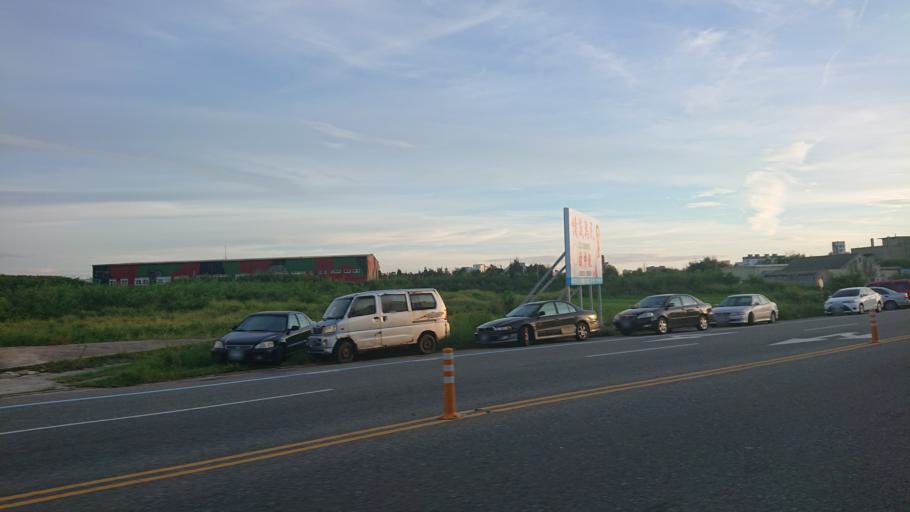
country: TW
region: Taiwan
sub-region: Penghu
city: Ma-kung
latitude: 23.5692
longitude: 119.5889
